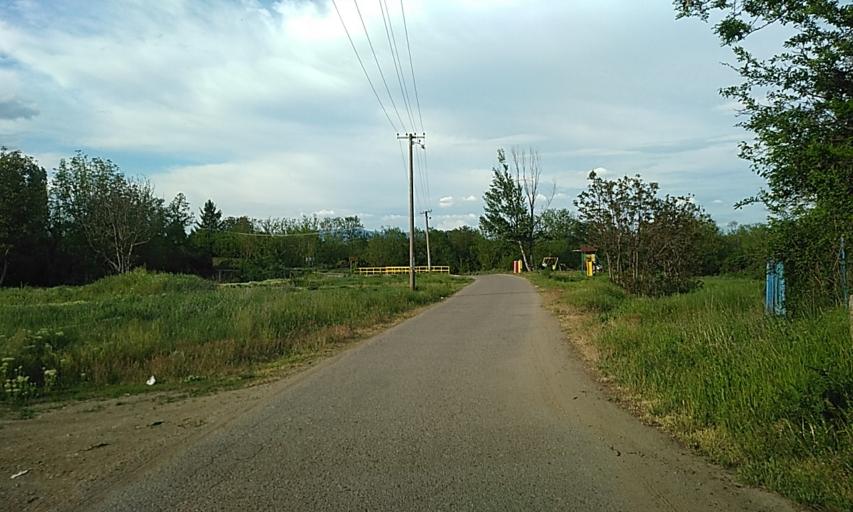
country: RS
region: Central Serbia
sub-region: Nisavski Okrug
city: Aleksinac
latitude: 43.4379
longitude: 21.7327
